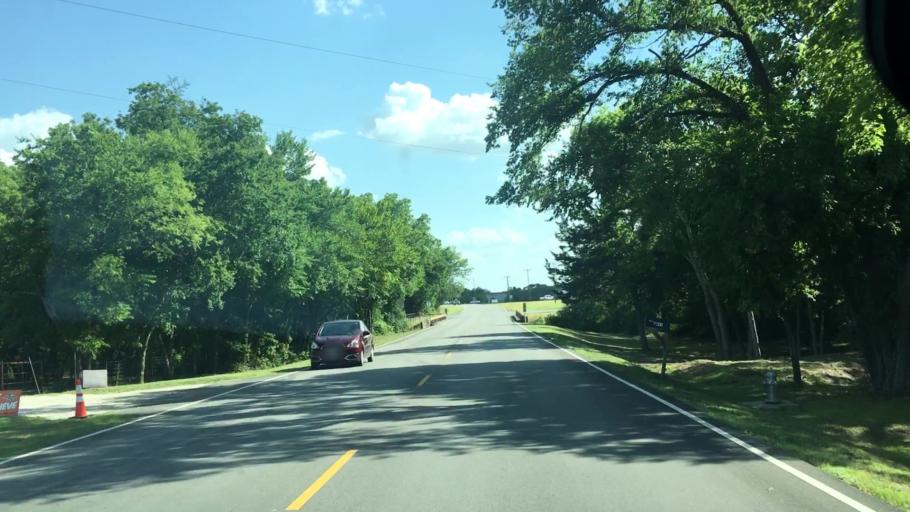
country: US
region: Texas
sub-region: Dallas County
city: Lancaster
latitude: 32.5882
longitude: -96.7515
